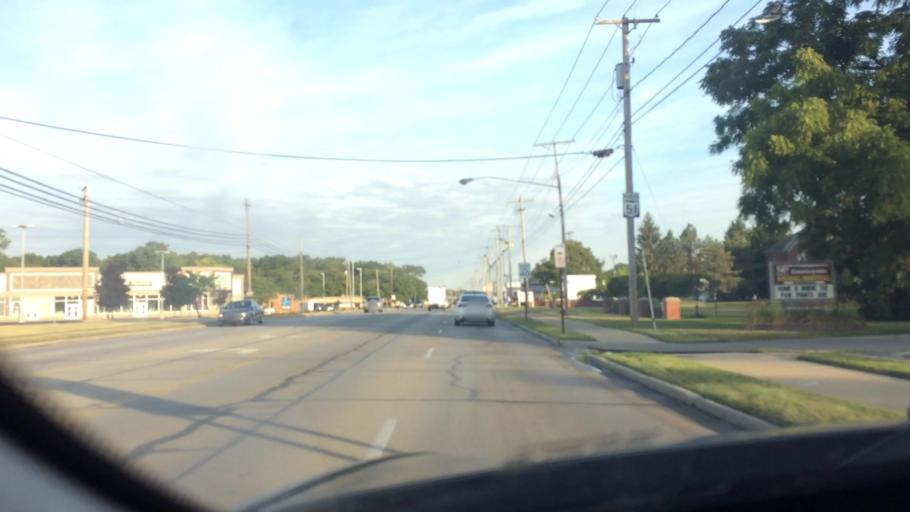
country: US
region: Ohio
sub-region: Lucas County
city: Ottawa Hills
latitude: 41.7066
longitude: -83.6662
